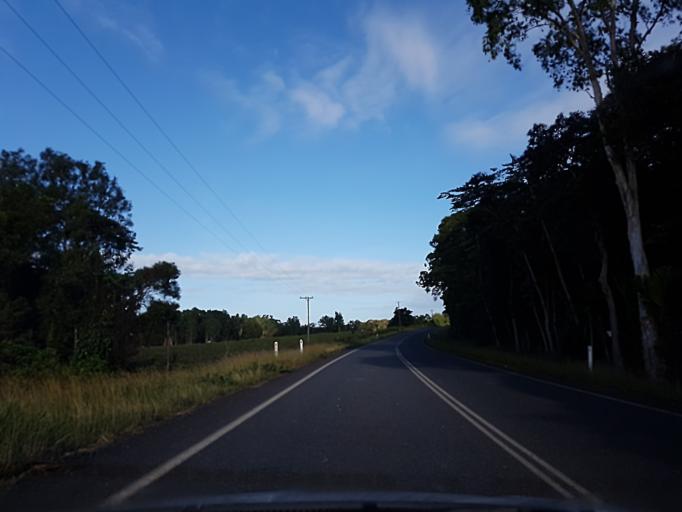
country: AU
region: Queensland
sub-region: Cairns
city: Port Douglas
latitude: -16.3206
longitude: 145.4063
